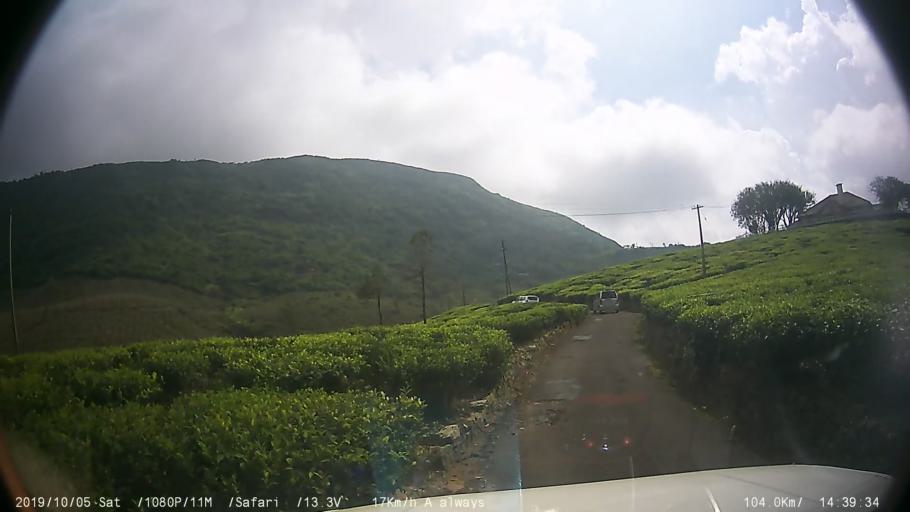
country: IN
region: Kerala
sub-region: Kottayam
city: Erattupetta
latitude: 9.6190
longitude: 76.9547
